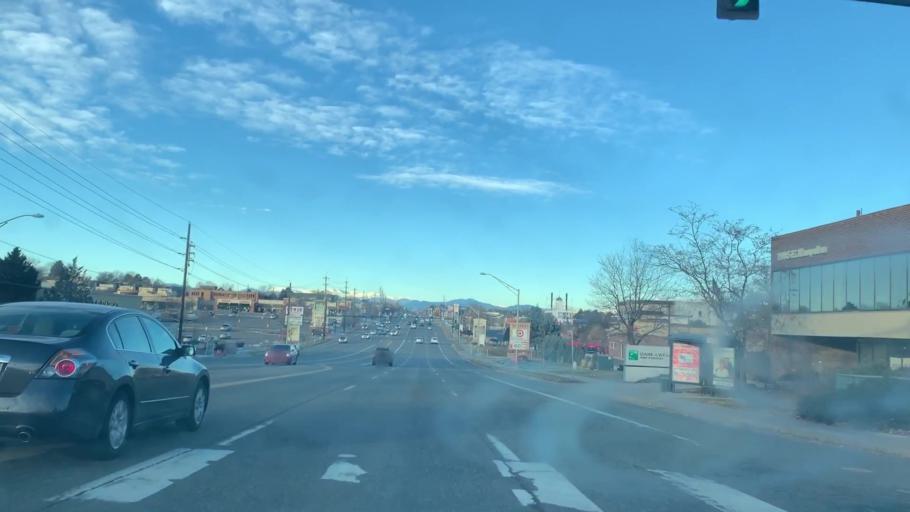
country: US
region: Colorado
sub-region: Arapahoe County
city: Cherry Hills Village
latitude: 39.6532
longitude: -104.8990
